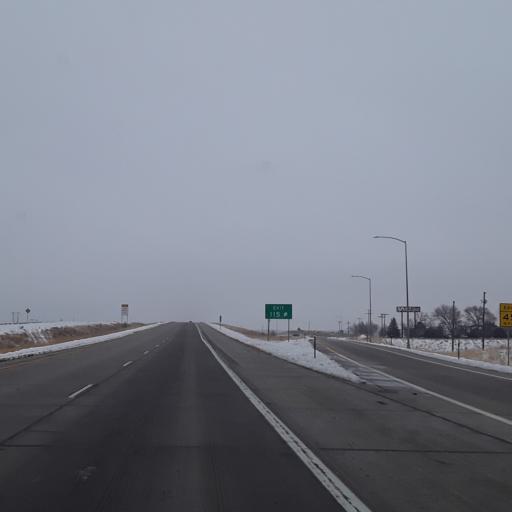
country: US
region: Colorado
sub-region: Logan County
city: Sterling
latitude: 40.4967
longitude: -103.2640
